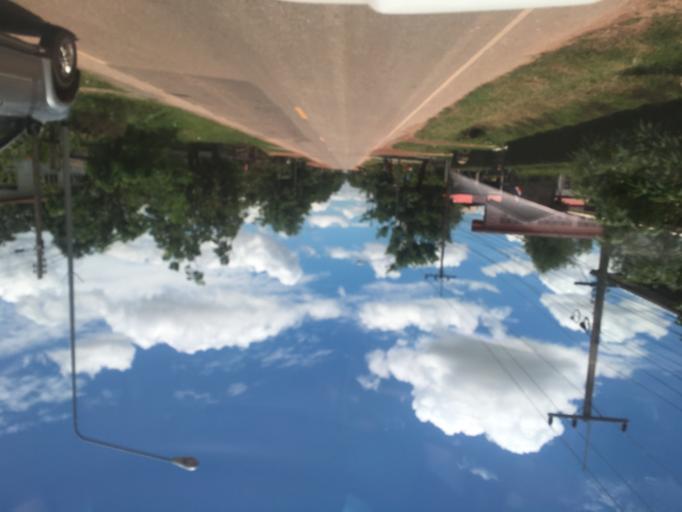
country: TH
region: Changwat Udon Thani
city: Nong Saeng
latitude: 17.1218
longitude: 102.8238
